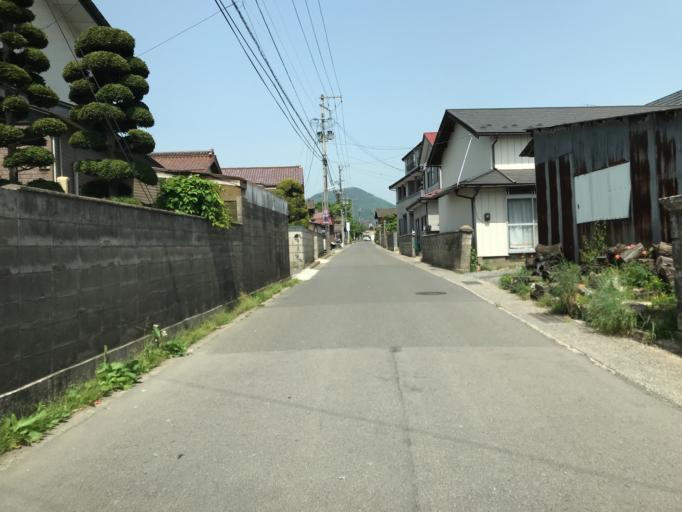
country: JP
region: Fukushima
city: Fukushima-shi
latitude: 37.8284
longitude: 140.4625
